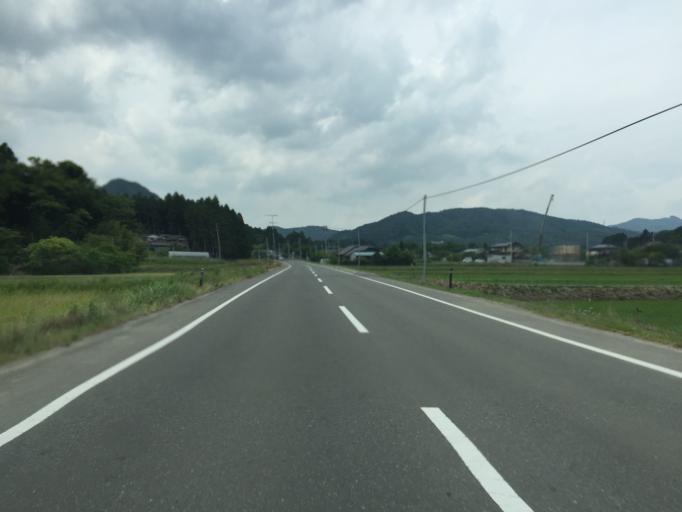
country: JP
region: Miyagi
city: Marumori
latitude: 37.8168
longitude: 140.8901
